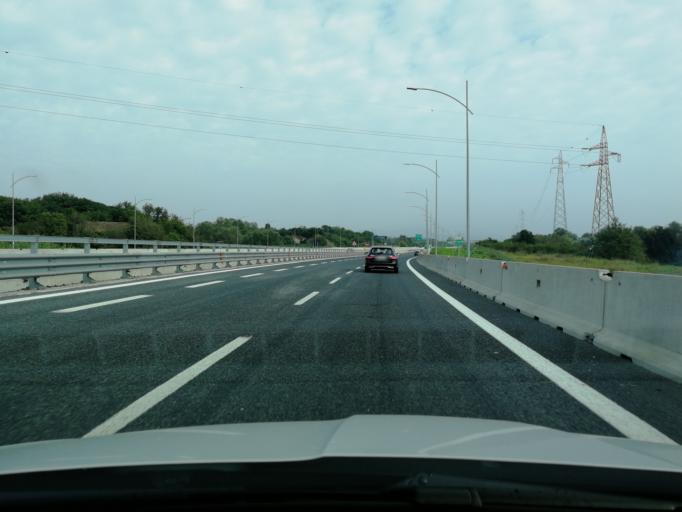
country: IT
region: Latium
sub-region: Citta metropolitana di Roma Capitale
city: Setteville
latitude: 41.9234
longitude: 12.6196
